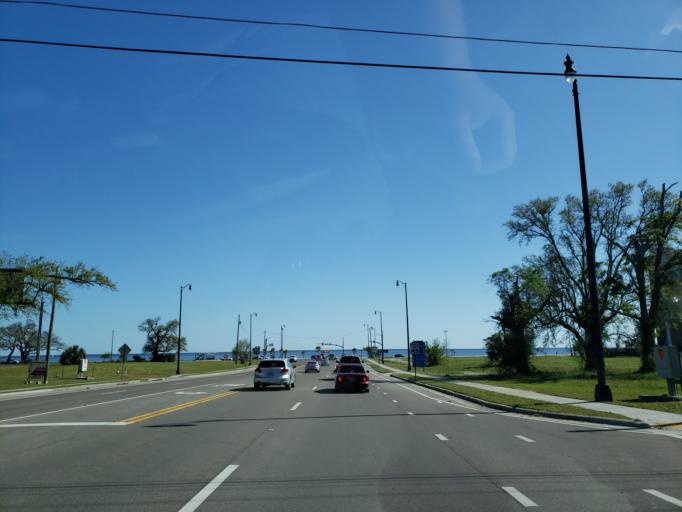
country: US
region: Mississippi
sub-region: Harrison County
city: Gulfport
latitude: 30.3843
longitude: -89.0270
